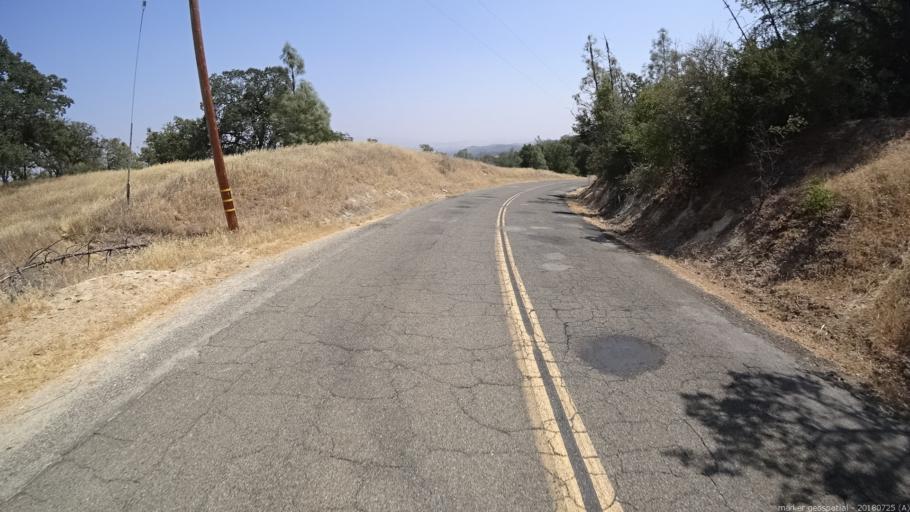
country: US
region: California
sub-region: San Luis Obispo County
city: San Miguel
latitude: 35.9213
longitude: -120.5324
